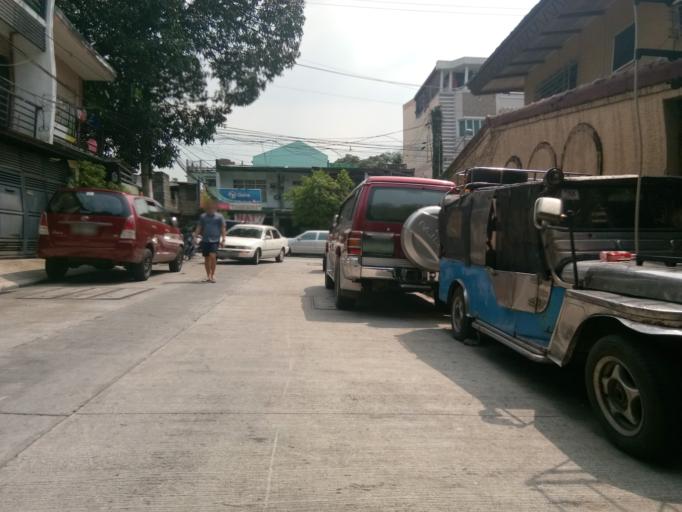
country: PH
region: Metro Manila
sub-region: San Juan
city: San Juan
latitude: 14.6130
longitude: 121.0525
